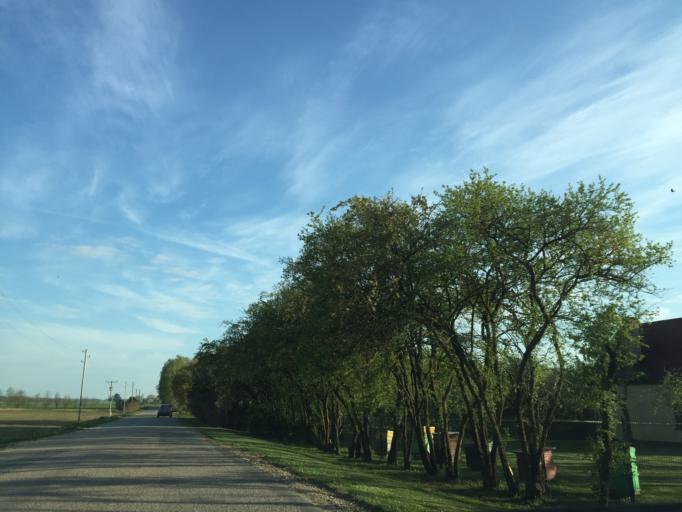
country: LV
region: Bauskas Rajons
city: Bauska
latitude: 56.3063
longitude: 24.2611
